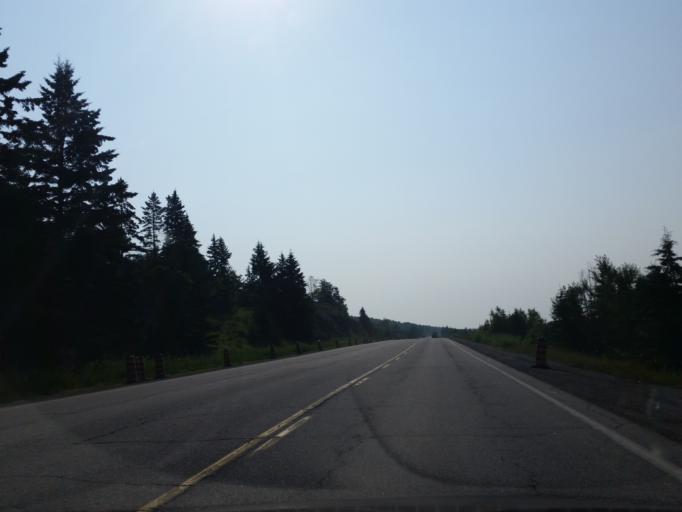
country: CA
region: Ontario
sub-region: Nipissing District
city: North Bay
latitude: 46.4264
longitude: -80.1970
